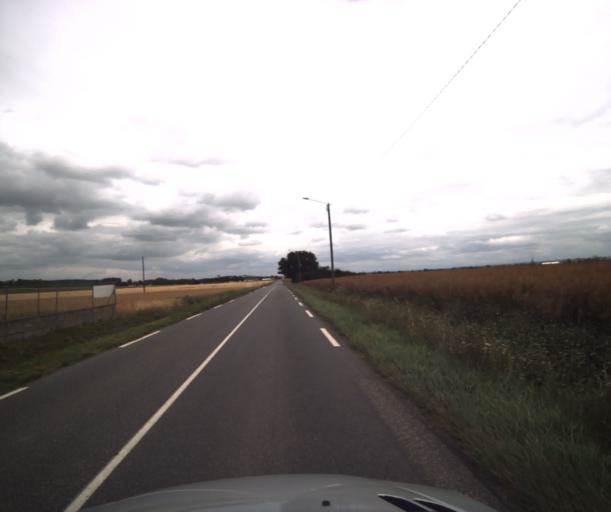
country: FR
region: Midi-Pyrenees
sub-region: Departement de la Haute-Garonne
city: Labarthe-sur-Leze
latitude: 43.4472
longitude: 1.4110
